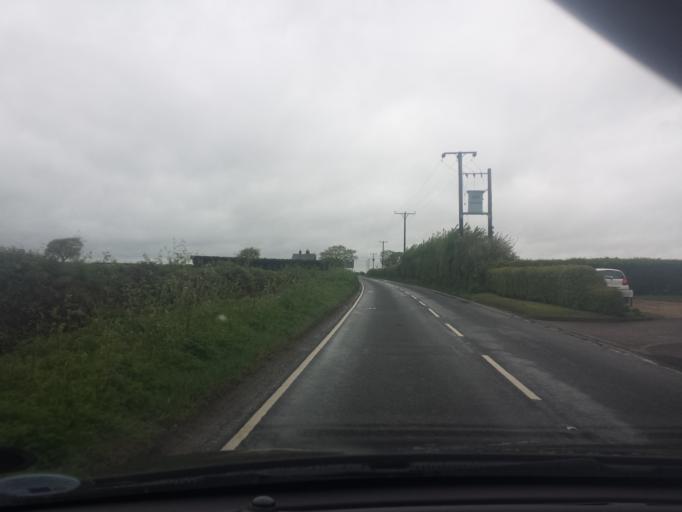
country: GB
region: England
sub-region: Essex
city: Alresford
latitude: 51.8967
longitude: 1.0228
